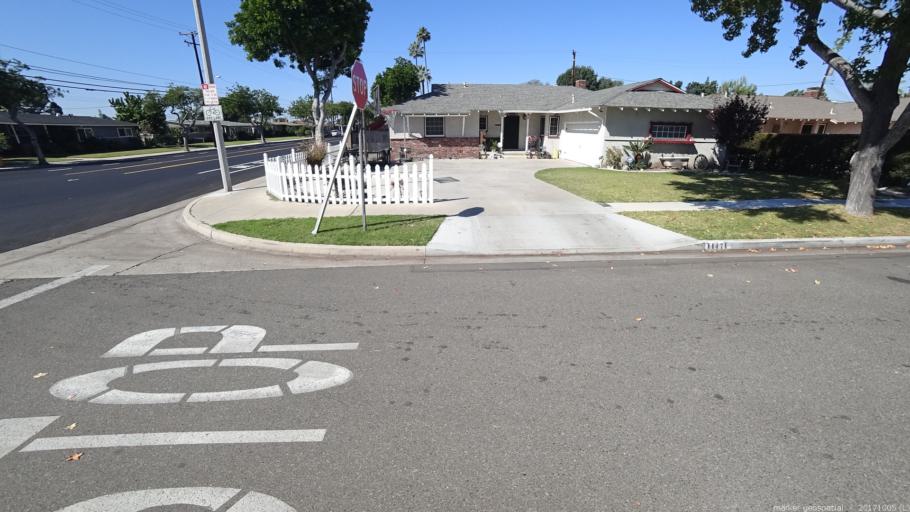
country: US
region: California
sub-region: Orange County
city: Stanton
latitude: 33.7959
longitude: -117.9723
